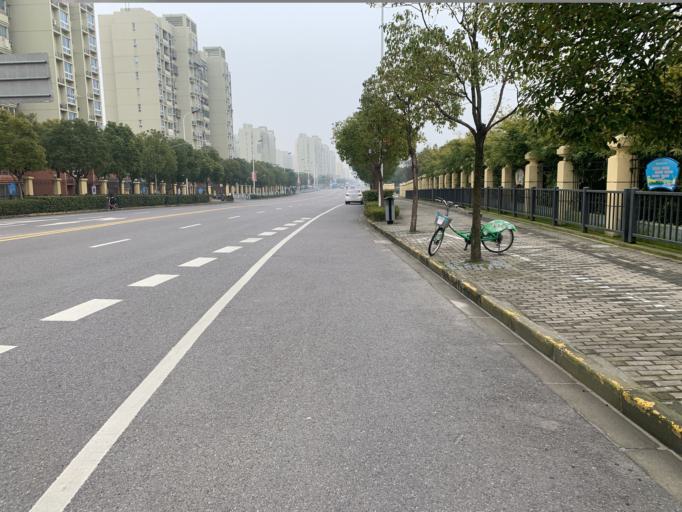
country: CN
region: Shanghai Shi
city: Huamu
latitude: 31.2412
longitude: 121.6222
